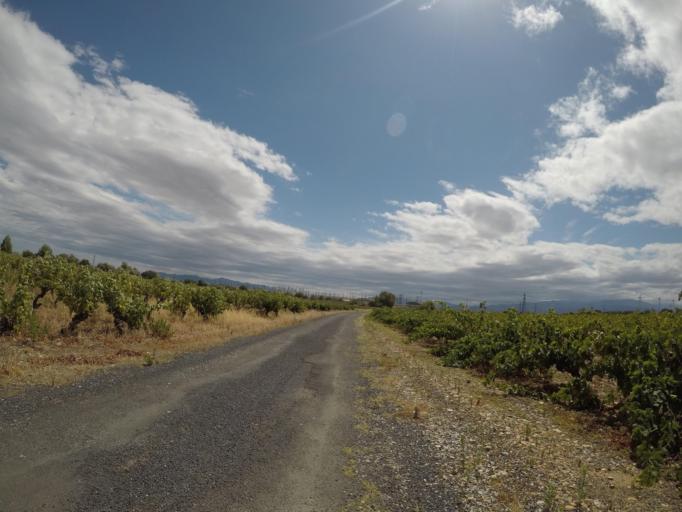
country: FR
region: Languedoc-Roussillon
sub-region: Departement des Pyrenees-Orientales
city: Baixas
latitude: 42.7376
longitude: 2.8029
